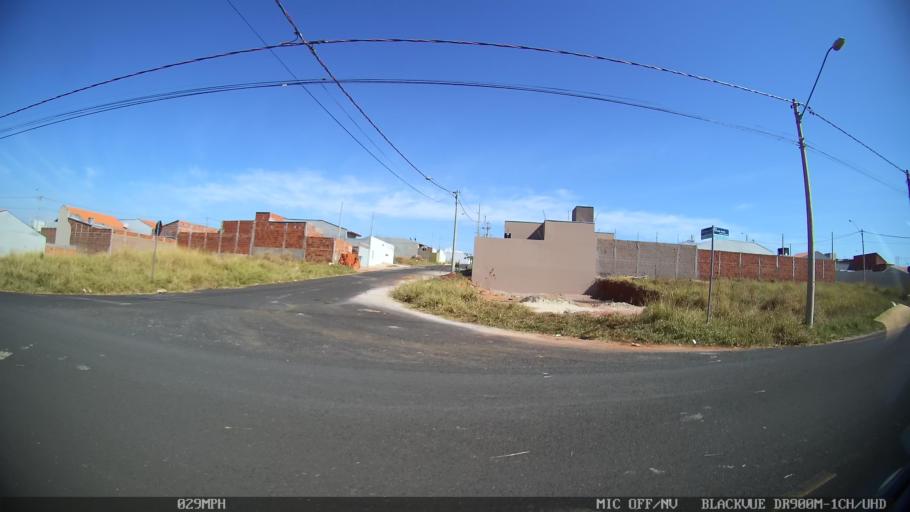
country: BR
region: Sao Paulo
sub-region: Sao Jose Do Rio Preto
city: Sao Jose do Rio Preto
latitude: -20.7554
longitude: -49.4218
